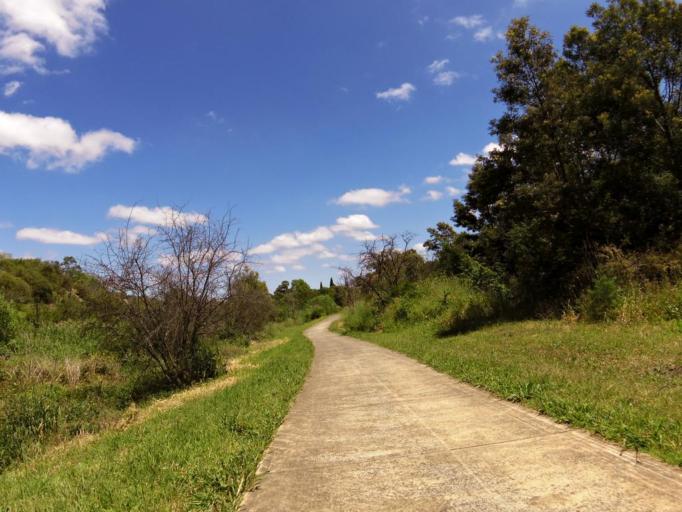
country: AU
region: Victoria
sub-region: Moreland
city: Fawkner
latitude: -37.7193
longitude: 144.9776
